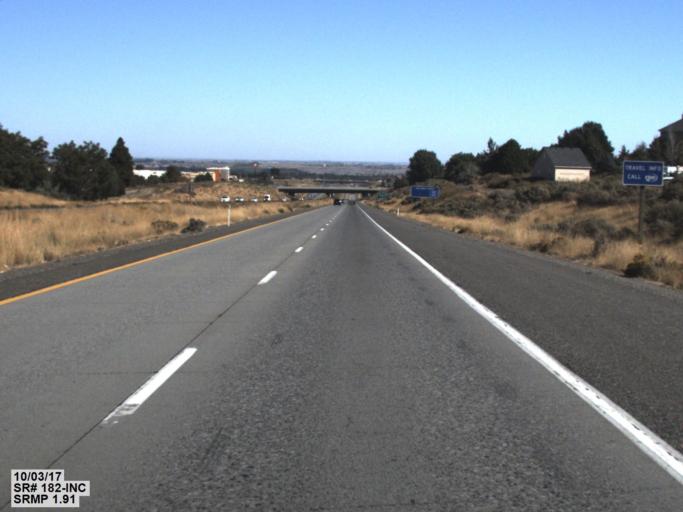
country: US
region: Washington
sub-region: Benton County
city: Richland
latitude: 46.2481
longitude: -119.3234
